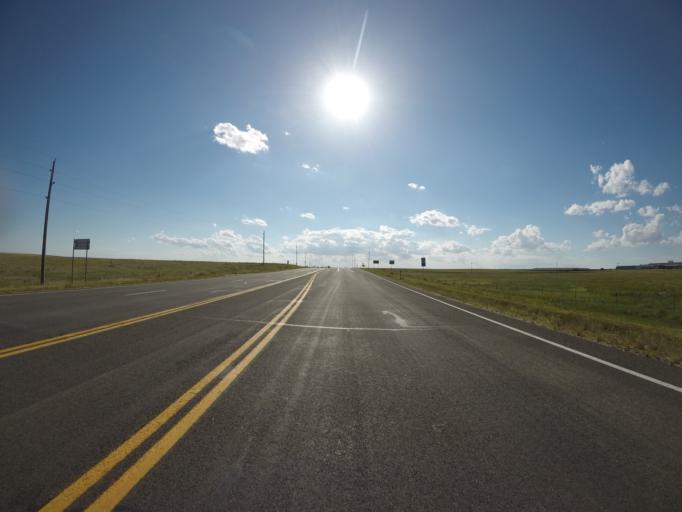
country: US
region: Colorado
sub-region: Morgan County
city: Fort Morgan
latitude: 40.6114
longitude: -103.7992
